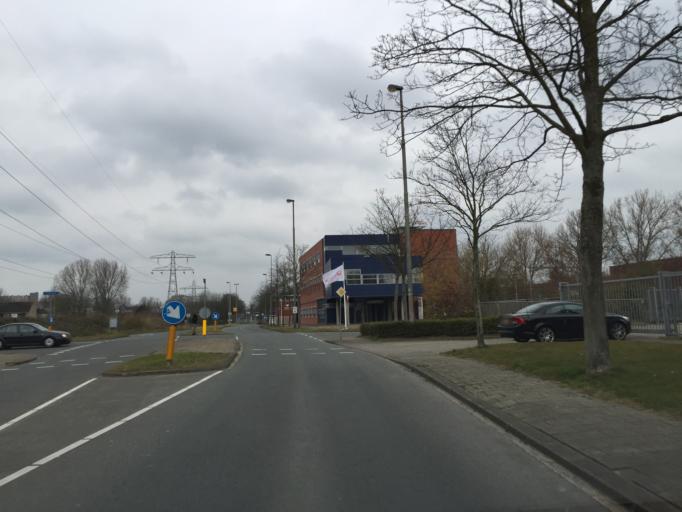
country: NL
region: South Holland
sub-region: Gemeente Delft
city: Delft
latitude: 51.9849
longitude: 4.3671
